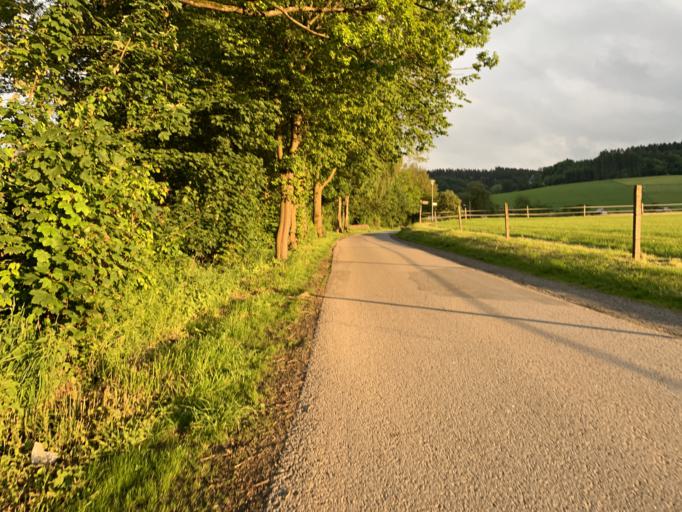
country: DE
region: North Rhine-Westphalia
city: Eslohe
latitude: 51.2849
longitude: 8.1721
